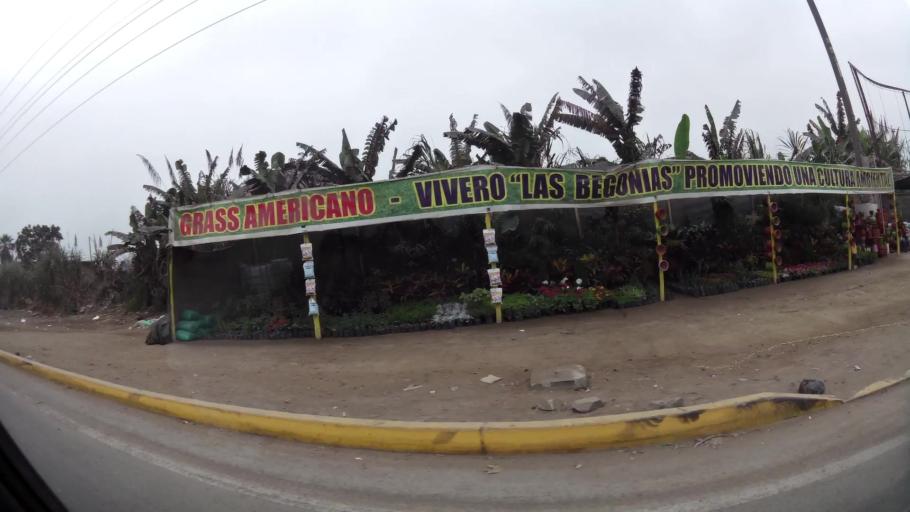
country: PE
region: Lima
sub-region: Lima
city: Urb. Santo Domingo
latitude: -11.8741
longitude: -77.0691
